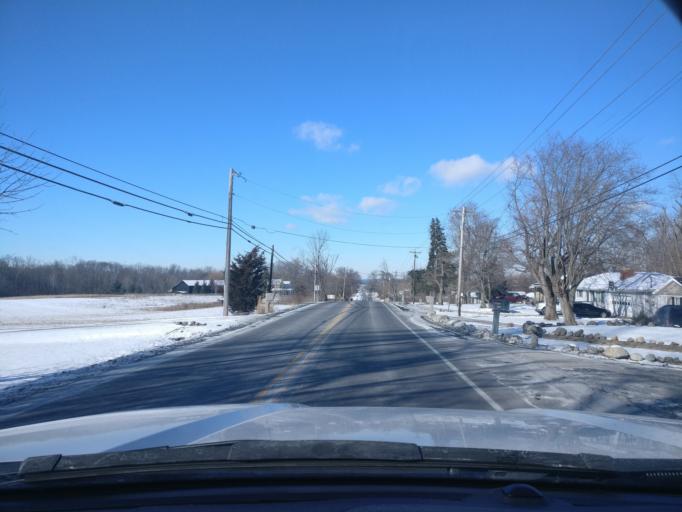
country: US
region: Ohio
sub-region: Warren County
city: Hunter
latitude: 39.5268
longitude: -84.2799
